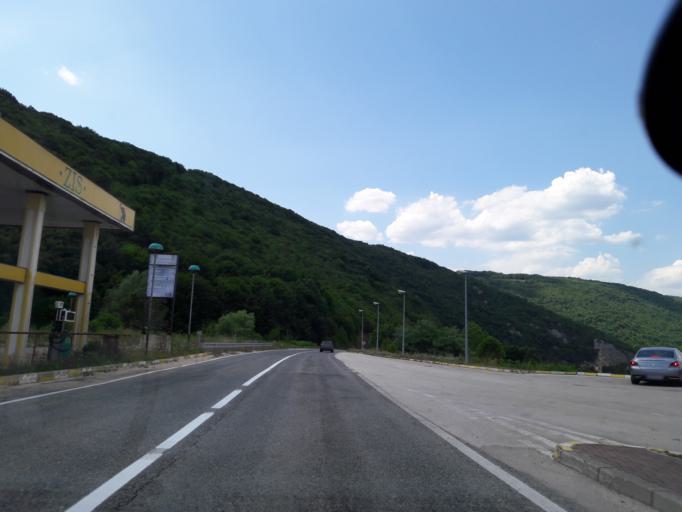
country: BA
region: Republika Srpska
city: Mrkonjic Grad
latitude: 44.4891
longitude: 17.1594
